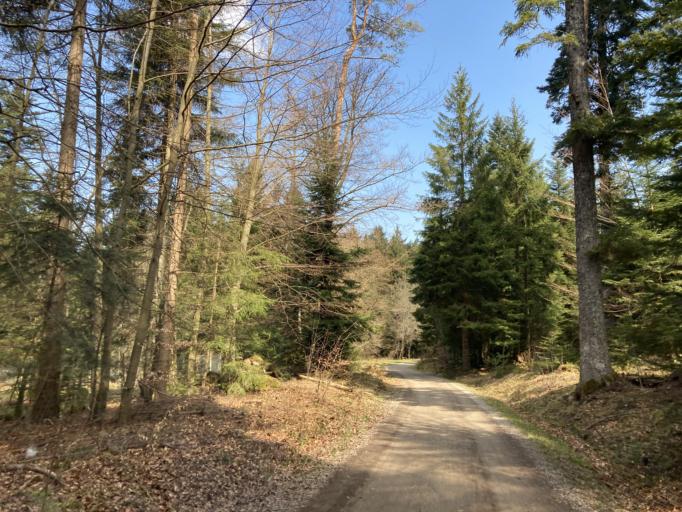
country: DE
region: Baden-Wuerttemberg
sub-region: Karlsruhe Region
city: Schomberg
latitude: 48.7865
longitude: 8.6281
